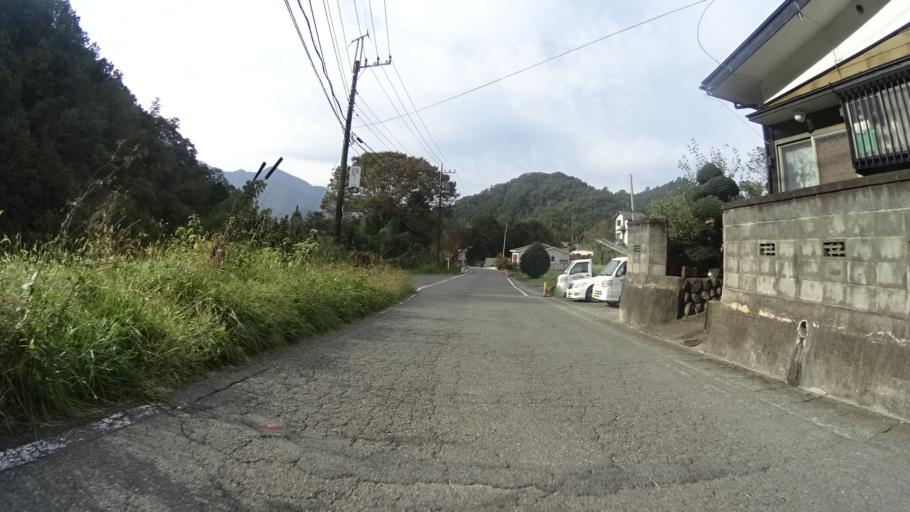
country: JP
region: Yamanashi
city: Otsuki
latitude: 35.6150
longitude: 139.0162
